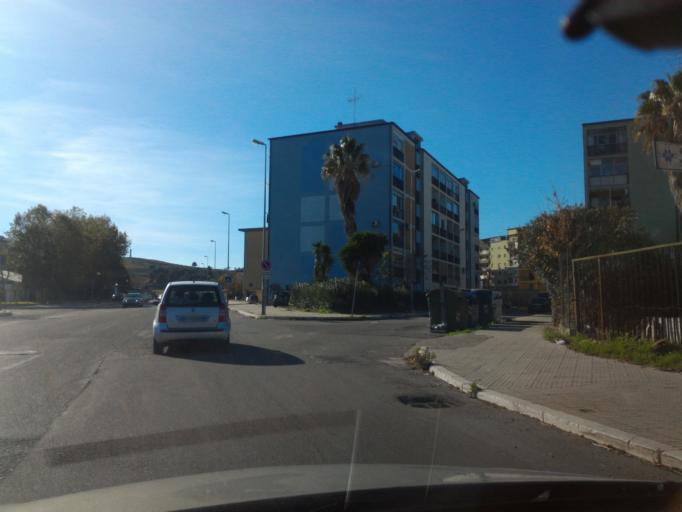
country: IT
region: Calabria
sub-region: Provincia di Crotone
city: Crotone
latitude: 39.0830
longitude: 17.1142
